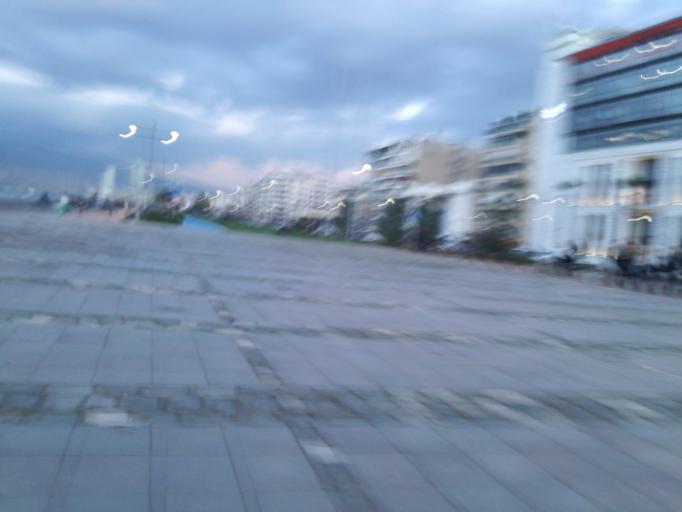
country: TR
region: Izmir
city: Izmir
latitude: 38.4316
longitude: 27.1354
